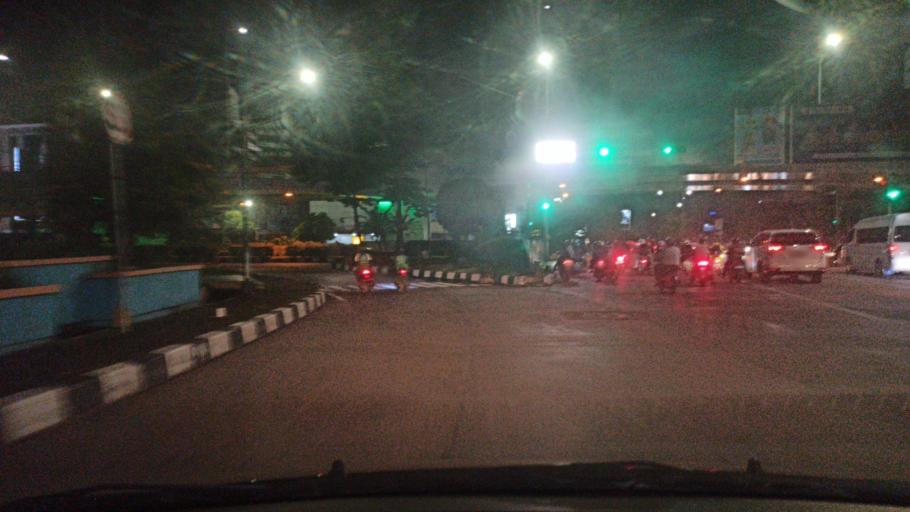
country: ID
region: South Sumatra
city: Palembang
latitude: -2.9610
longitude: 104.7378
